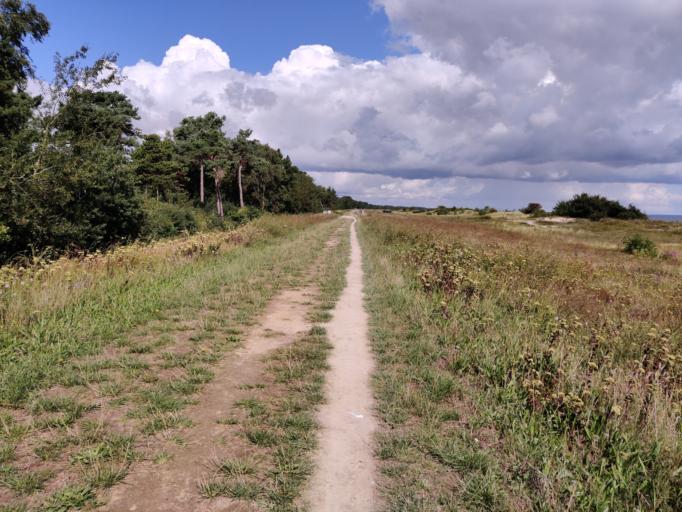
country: DK
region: Zealand
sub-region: Guldborgsund Kommune
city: Nykobing Falster
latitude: 54.6547
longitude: 11.9597
